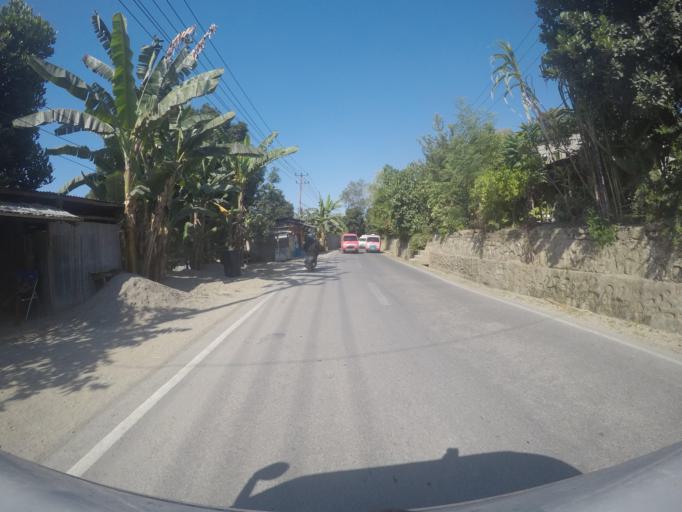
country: TL
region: Dili
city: Dili
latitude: -8.5657
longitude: 125.5518
